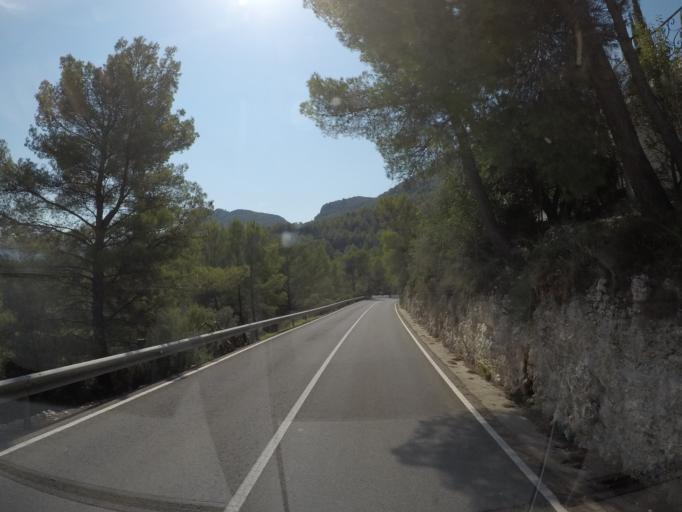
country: ES
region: Valencia
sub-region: Provincia de Alicante
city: Orba
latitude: 38.7813
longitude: -0.0792
